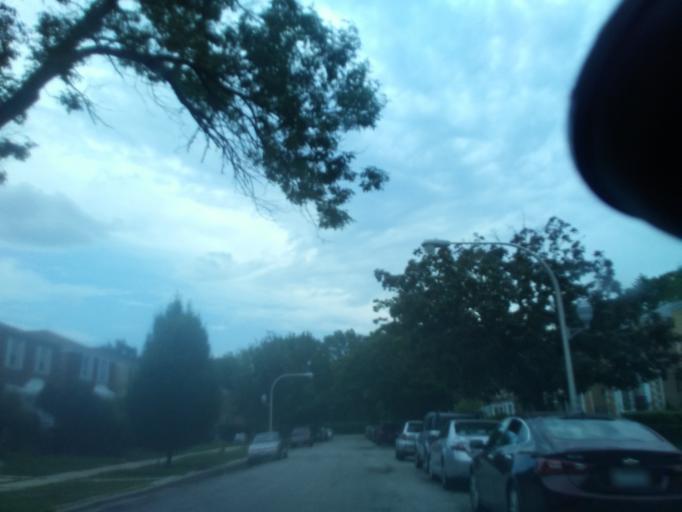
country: US
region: Illinois
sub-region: Cook County
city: Lincolnwood
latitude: 41.9948
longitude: -87.7227
